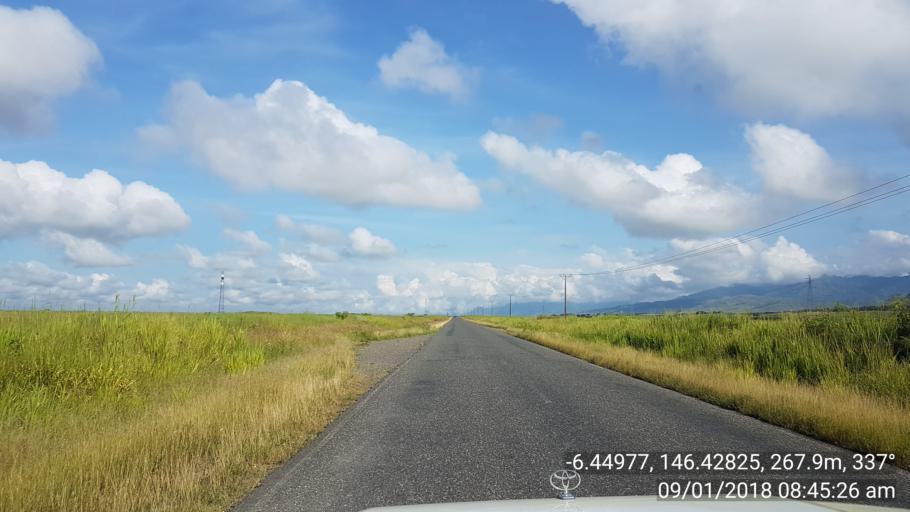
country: PG
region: Eastern Highlands
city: Kainantu
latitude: -6.4495
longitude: 146.4282
